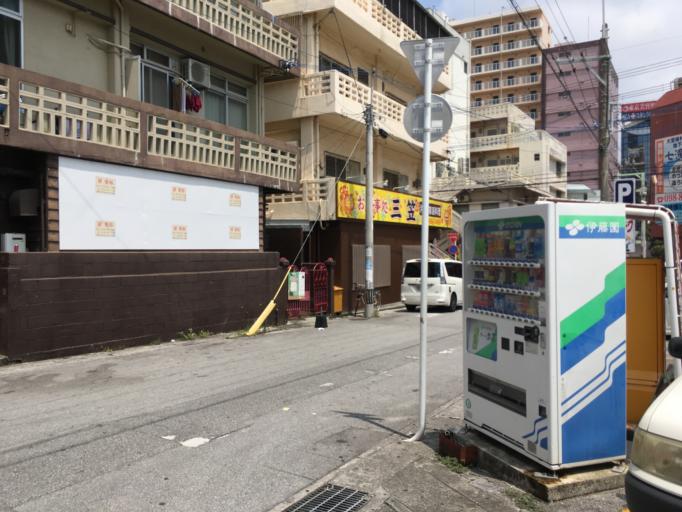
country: JP
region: Okinawa
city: Naha-shi
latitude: 26.2177
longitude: 127.6788
